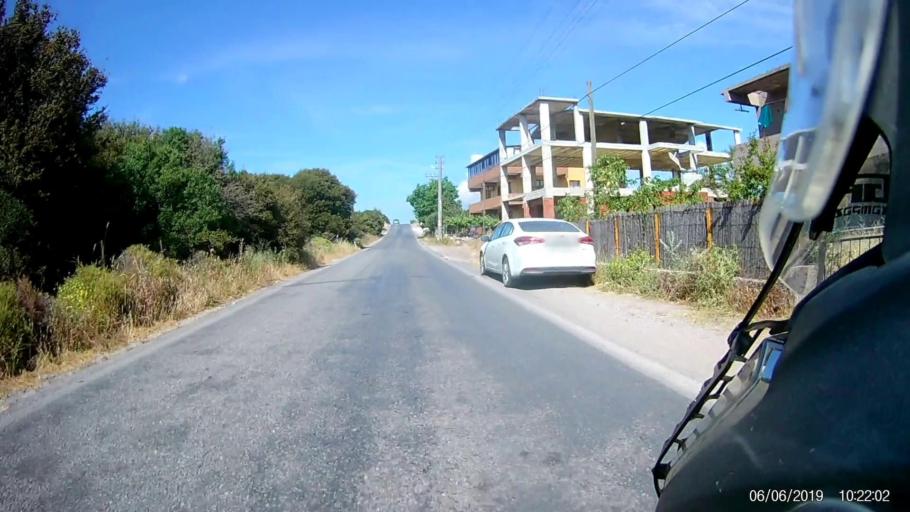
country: TR
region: Canakkale
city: Ayvacik
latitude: 39.5137
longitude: 26.4352
